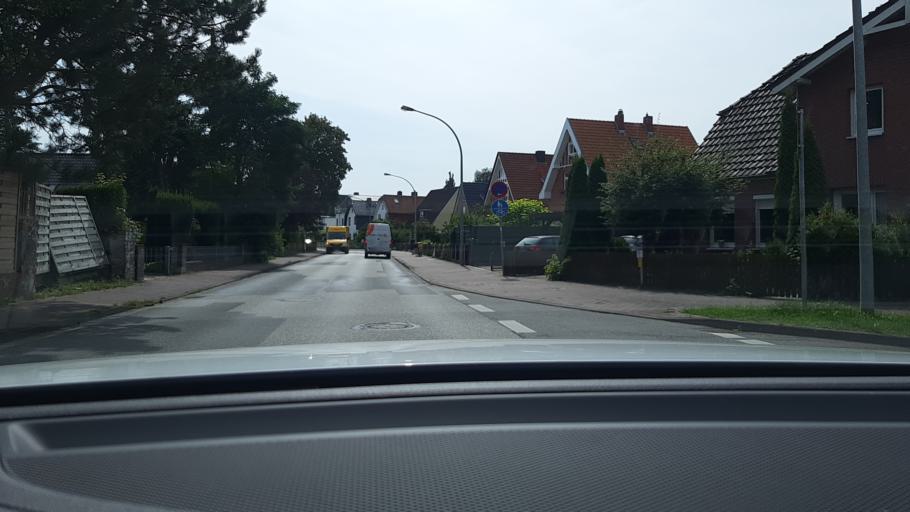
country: DE
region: Schleswig-Holstein
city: Stockelsdorf
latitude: 53.8948
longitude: 10.6517
